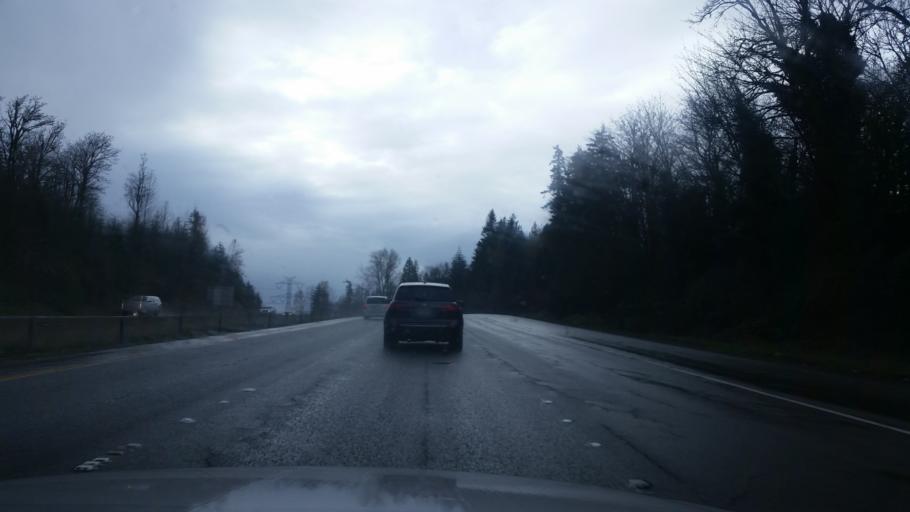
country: US
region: Washington
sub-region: King County
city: Covington
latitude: 47.3464
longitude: -122.1420
